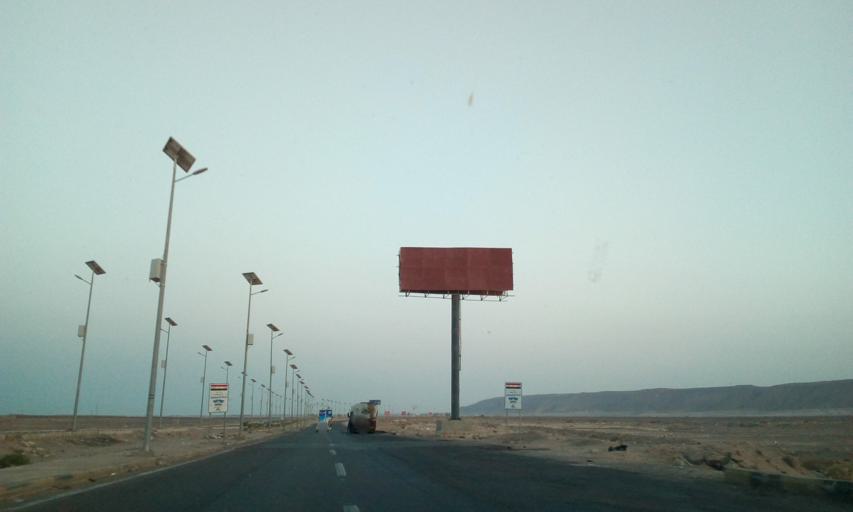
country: EG
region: Red Sea
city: El Gouna
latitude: 27.4179
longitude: 33.6167
